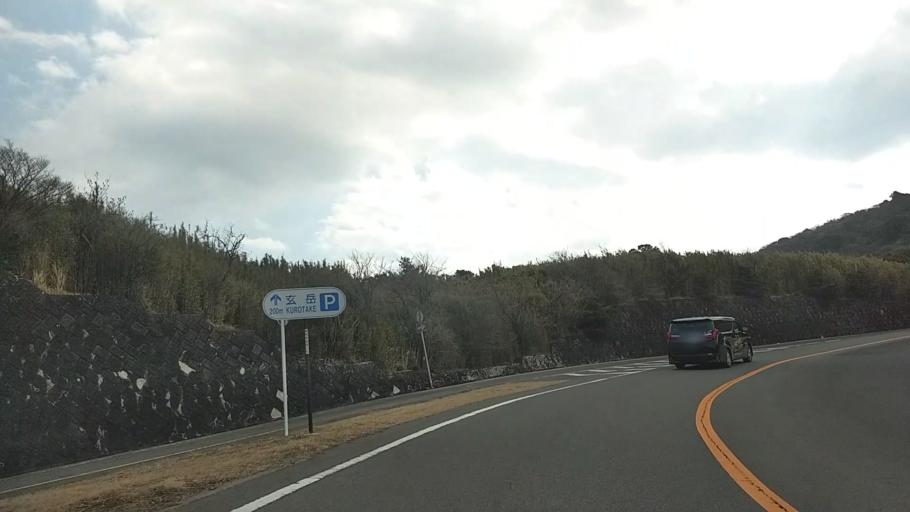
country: JP
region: Shizuoka
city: Atami
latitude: 35.0848
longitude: 139.0333
